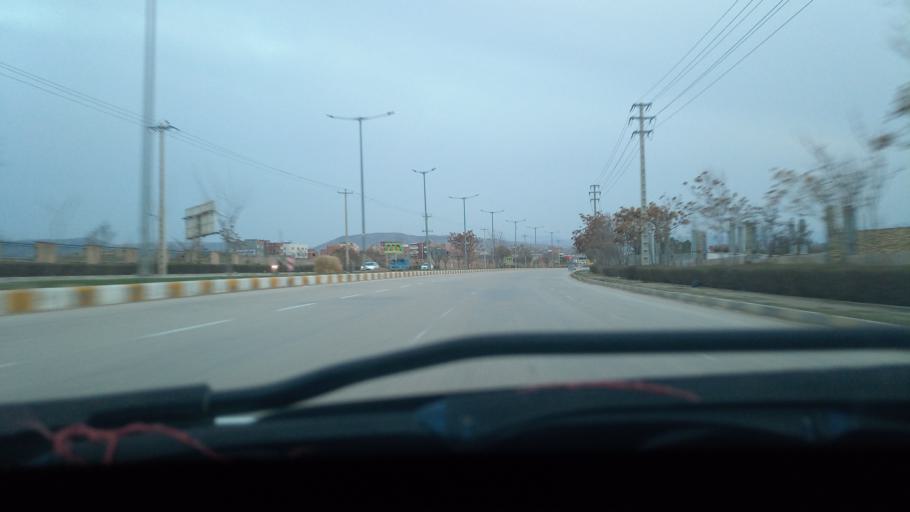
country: IR
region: Khorasan-e Shomali
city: Bojnurd
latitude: 37.4439
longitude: 57.3163
